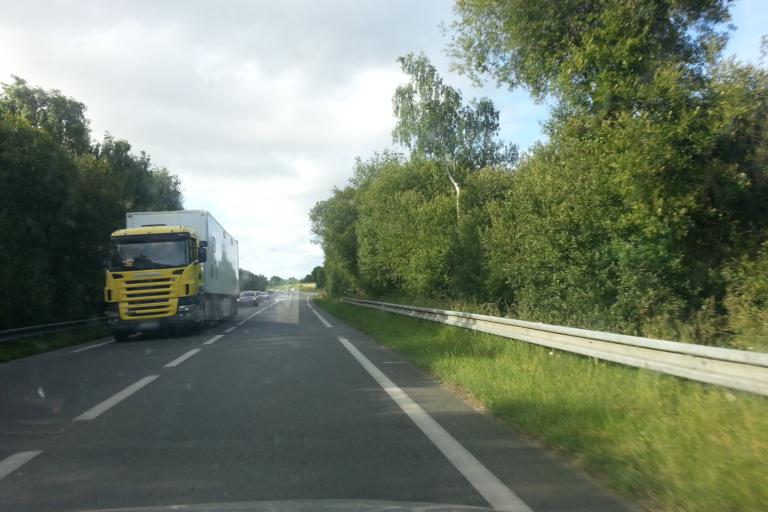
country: FR
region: Brittany
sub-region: Departement du Morbihan
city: Merlevenez
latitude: 47.7265
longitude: -3.2302
